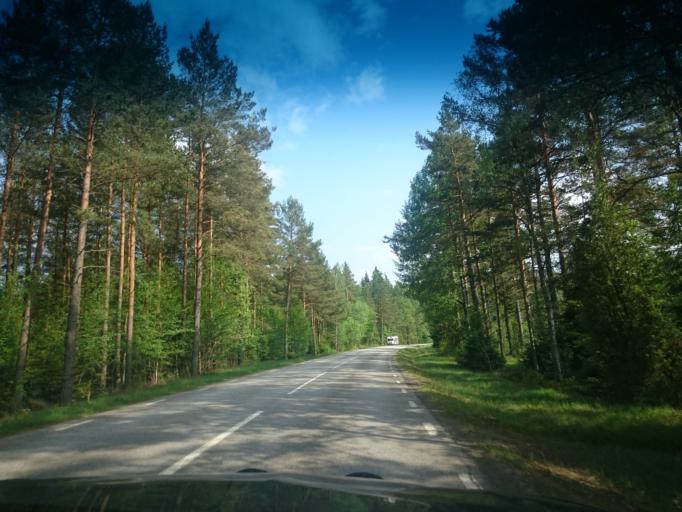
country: SE
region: Joenkoeping
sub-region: Vetlanda Kommun
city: Vetlanda
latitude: 57.3628
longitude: 15.0659
